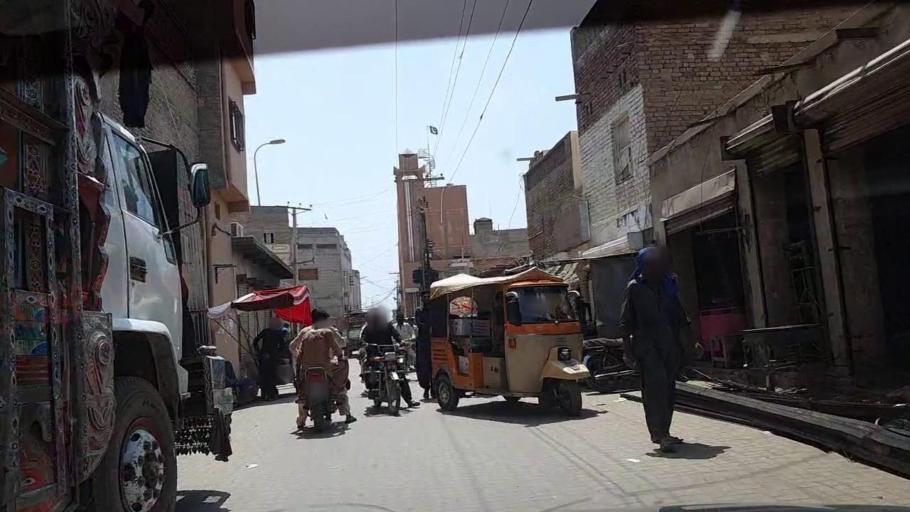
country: PK
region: Sindh
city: Khanpur
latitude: 27.8421
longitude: 69.4132
